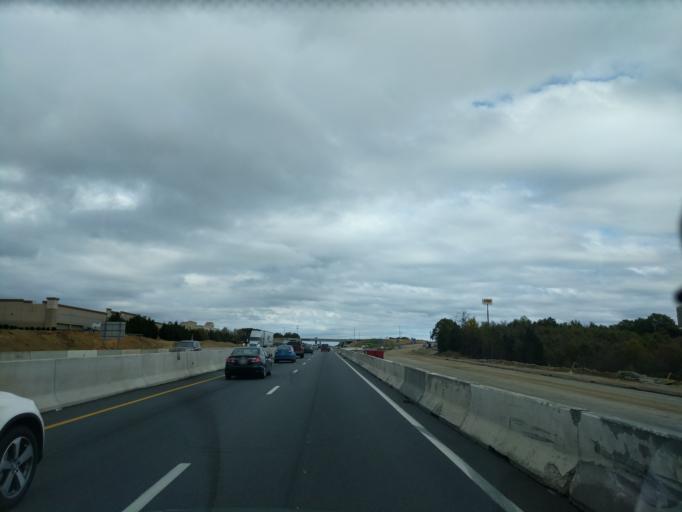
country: US
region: North Carolina
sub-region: Cabarrus County
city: Kannapolis
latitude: 35.4595
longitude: -80.5910
